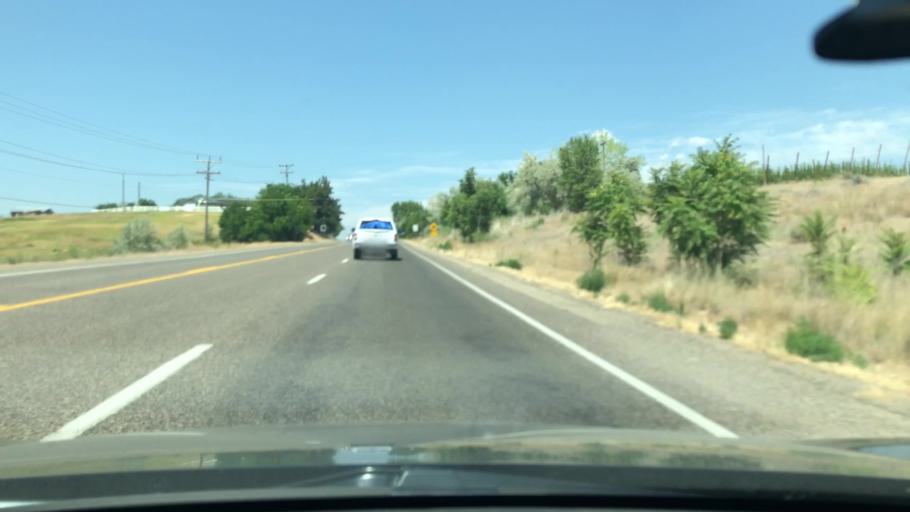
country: US
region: Idaho
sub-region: Canyon County
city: Wilder
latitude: 43.6578
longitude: -116.9117
